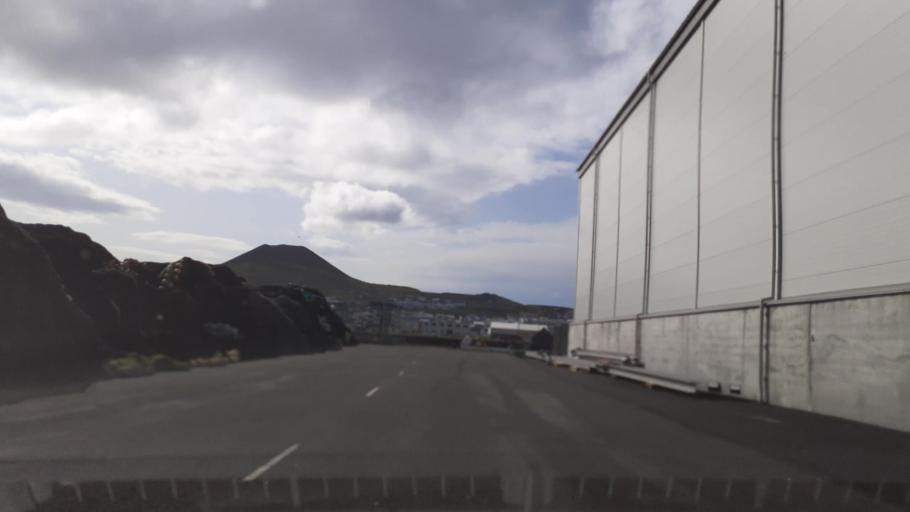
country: IS
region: South
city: Vestmannaeyjar
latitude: 63.4468
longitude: -20.2708
